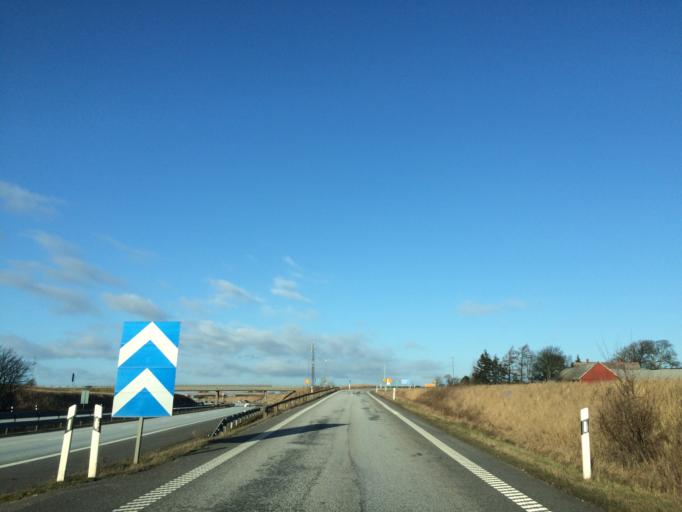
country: SE
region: Skane
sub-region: Lomma Kommun
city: Lomma
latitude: 55.7206
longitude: 13.0913
